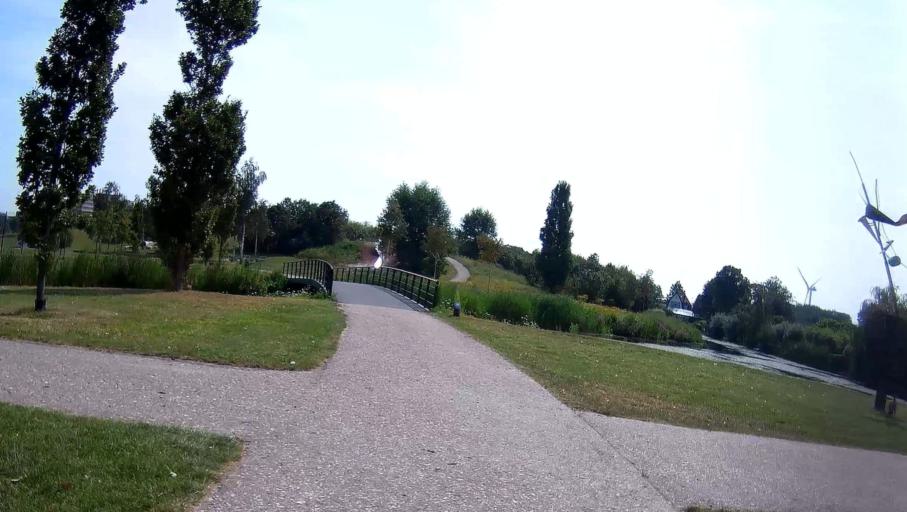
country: NL
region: South Holland
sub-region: Gemeente Leidschendam-Voorburg
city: Voorburg
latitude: 52.0801
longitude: 4.3807
